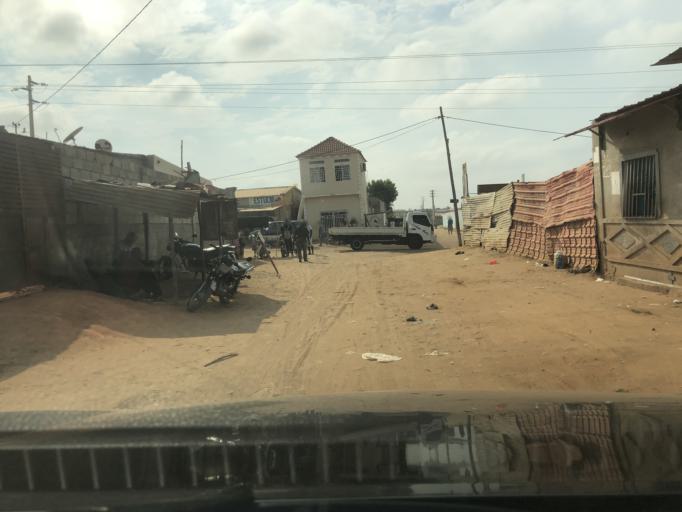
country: AO
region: Luanda
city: Luanda
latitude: -8.9372
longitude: 13.2390
